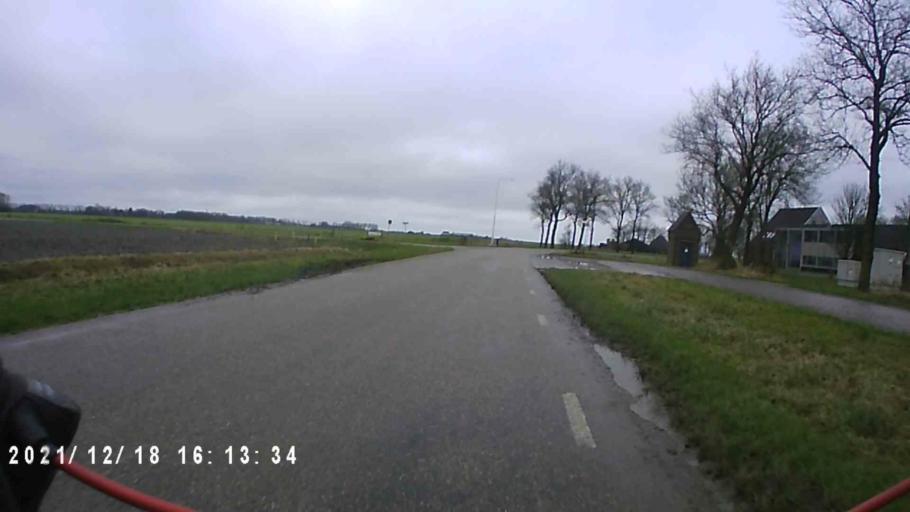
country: NL
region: Friesland
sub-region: Gemeente Dongeradeel
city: Anjum
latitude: 53.3686
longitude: 6.0687
